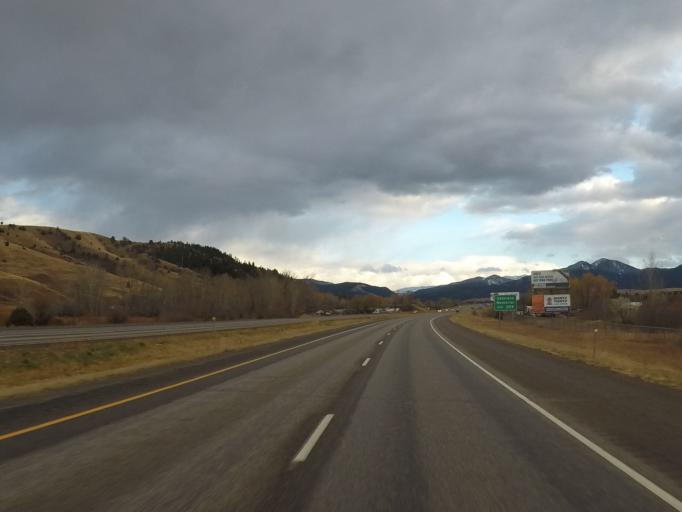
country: US
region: Montana
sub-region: Gallatin County
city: Bozeman
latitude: 45.6882
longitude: -111.0187
